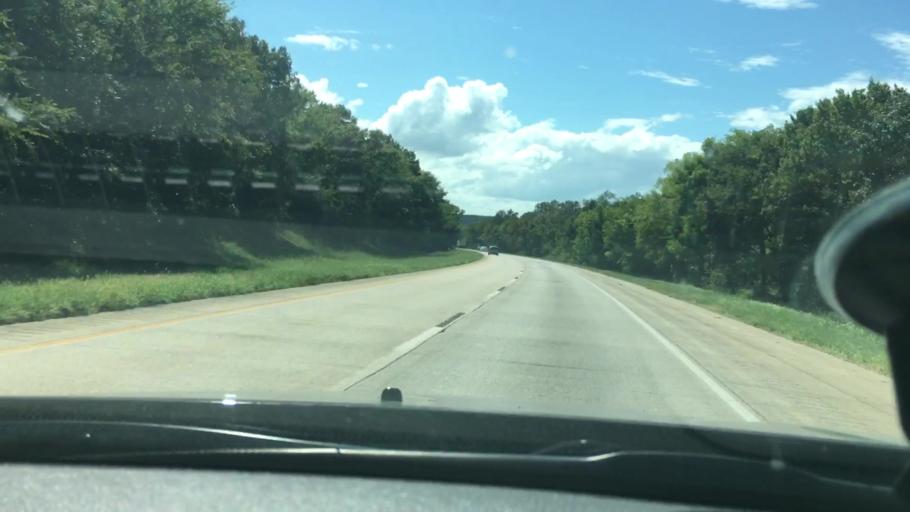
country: US
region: Oklahoma
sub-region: Sequoyah County
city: Vian
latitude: 35.4935
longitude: -95.0091
